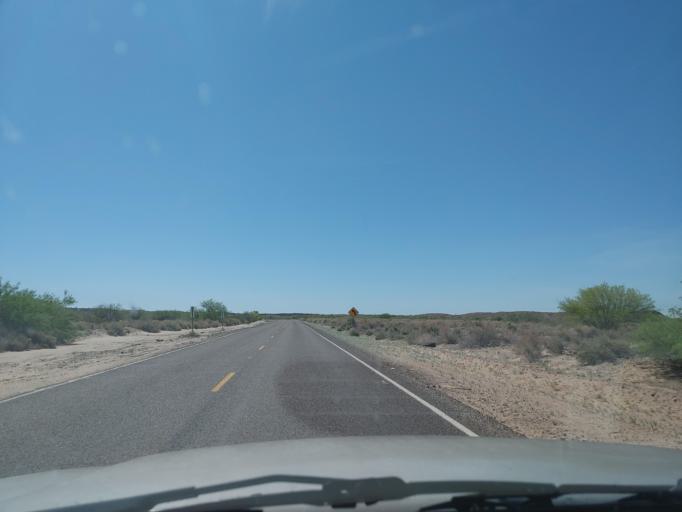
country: US
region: Arizona
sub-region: Maricopa County
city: Gila Bend
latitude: 32.9455
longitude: -113.3060
